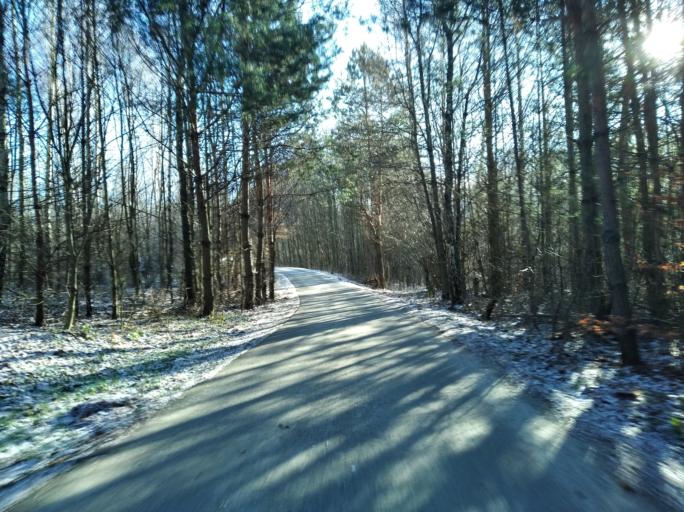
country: PL
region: Subcarpathian Voivodeship
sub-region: Powiat ropczycko-sedziszowski
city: Iwierzyce
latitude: 49.9593
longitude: 21.7528
